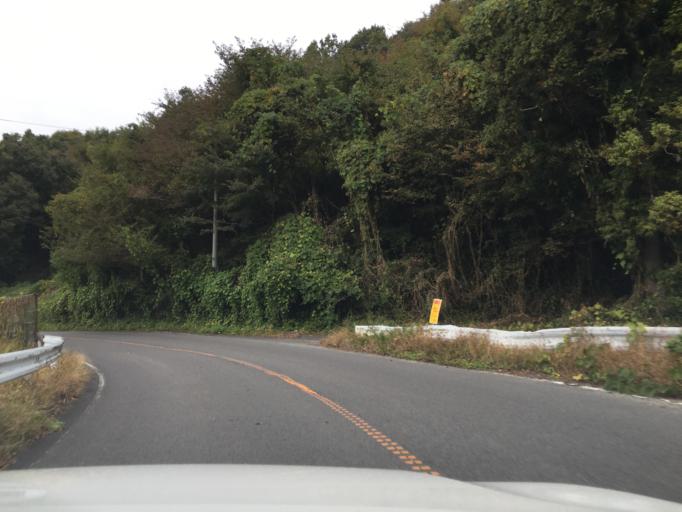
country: JP
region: Fukushima
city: Miharu
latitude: 37.4538
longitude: 140.5069
